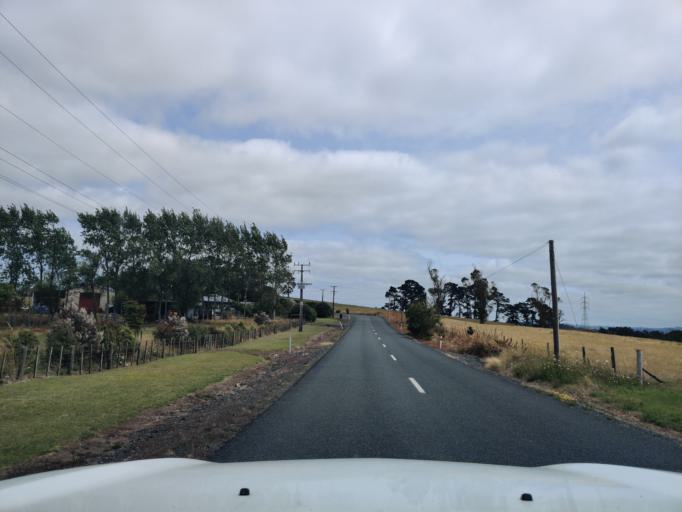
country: NZ
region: Waikato
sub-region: Waikato District
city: Te Kauwhata
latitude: -37.5128
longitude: 175.1764
